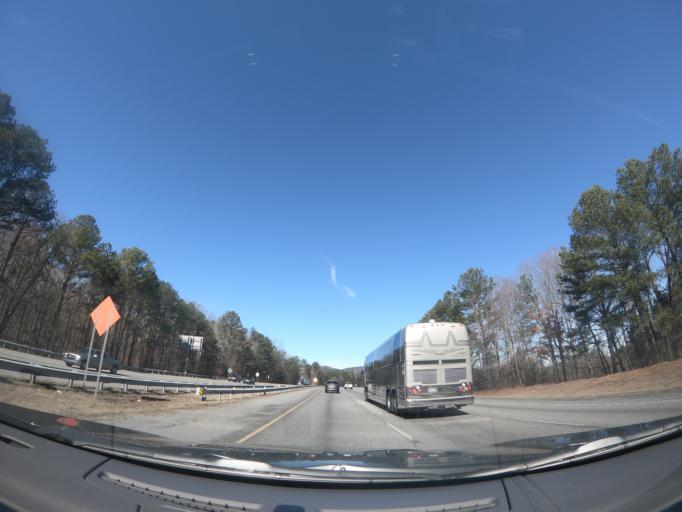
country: US
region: Georgia
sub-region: Whitfield County
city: Dalton
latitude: 34.6680
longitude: -84.9944
